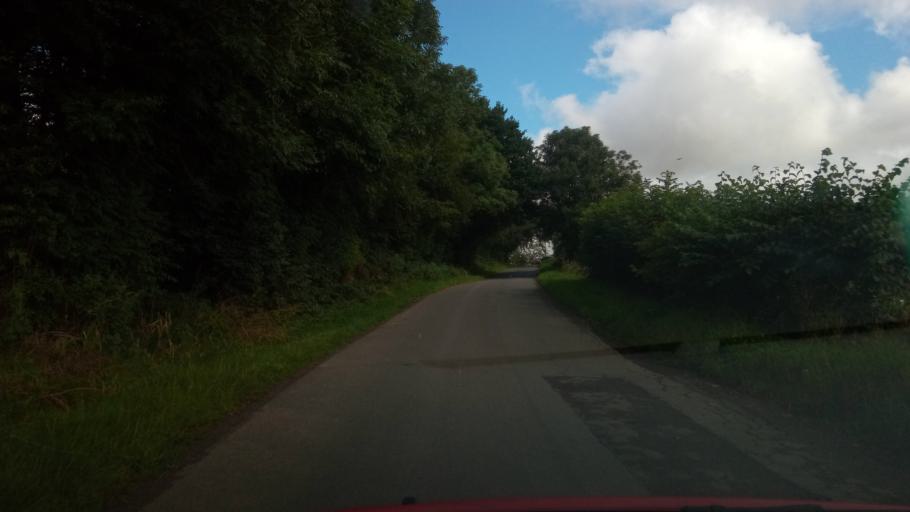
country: GB
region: Scotland
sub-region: The Scottish Borders
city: Earlston
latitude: 55.6434
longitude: -2.7006
